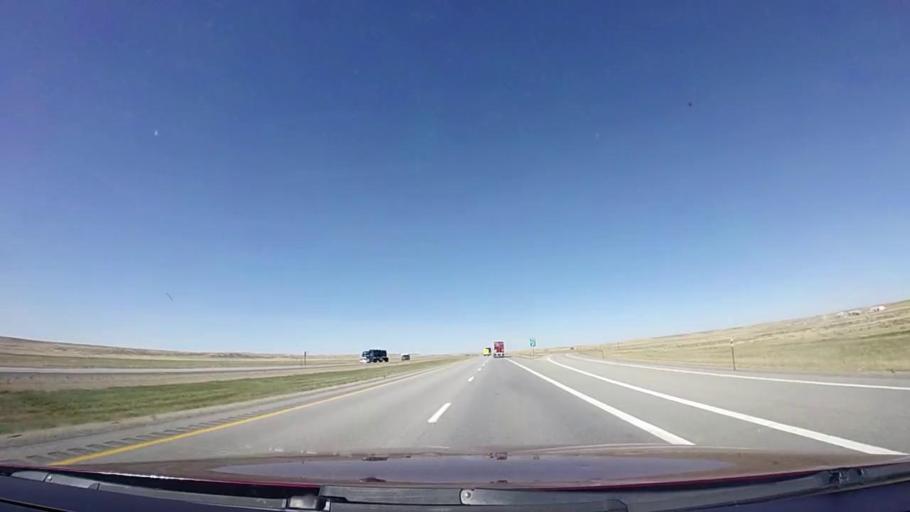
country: US
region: Wyoming
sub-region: Carbon County
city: Rawlins
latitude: 41.6662
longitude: -108.0273
